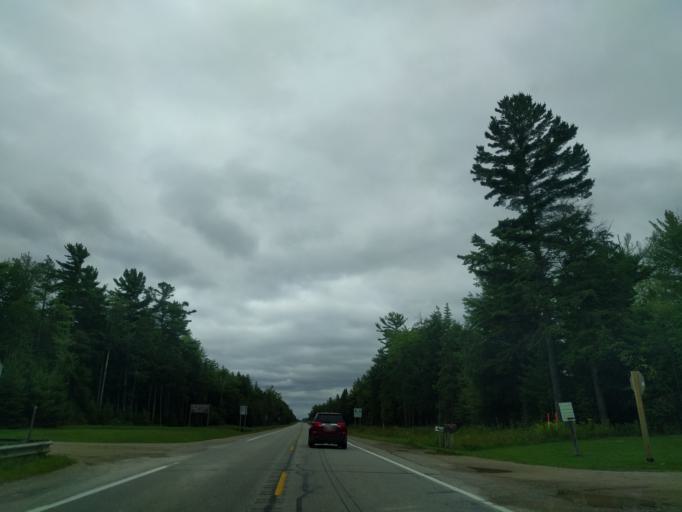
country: US
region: Michigan
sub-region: Delta County
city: Escanaba
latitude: 45.5782
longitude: -87.2461
